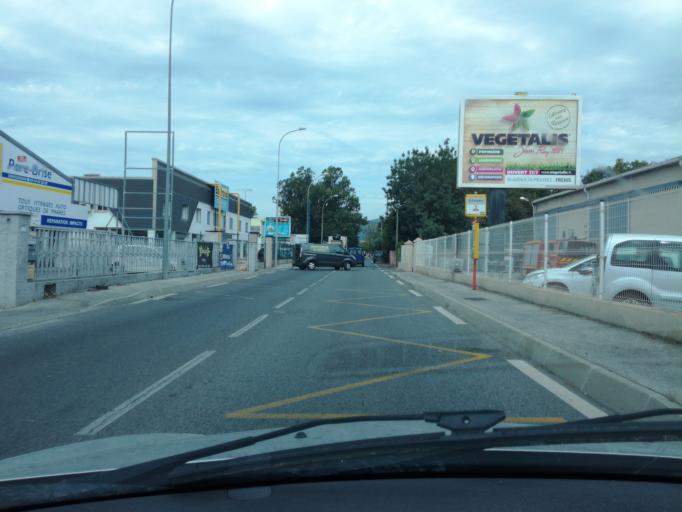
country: FR
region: Provence-Alpes-Cote d'Azur
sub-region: Departement du Var
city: Draguignan
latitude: 43.5227
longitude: 6.4642
